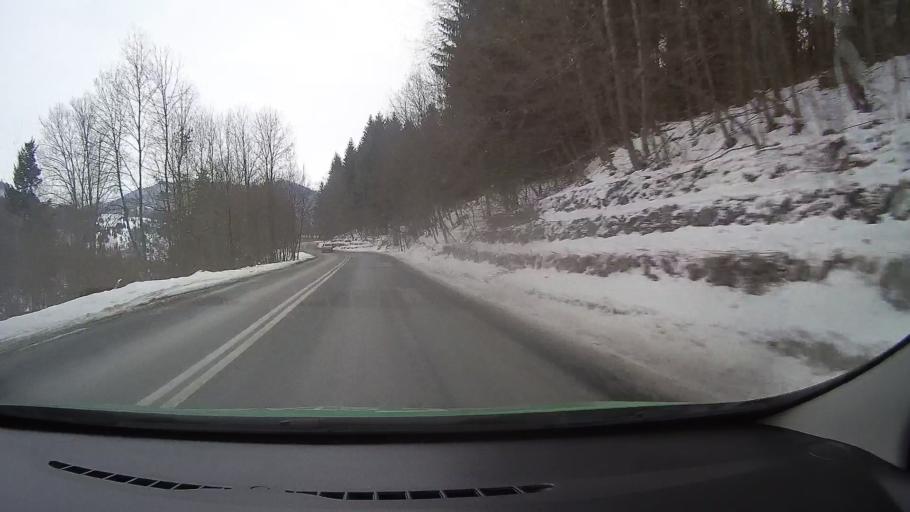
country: RO
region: Brasov
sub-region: Oras Predeal
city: Predeal
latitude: 45.5229
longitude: 25.5063
